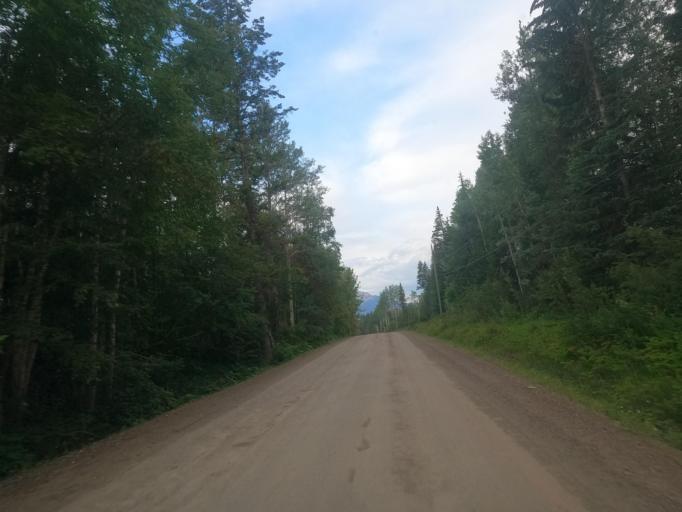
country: CA
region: British Columbia
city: Golden
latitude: 51.4458
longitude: -117.0149
